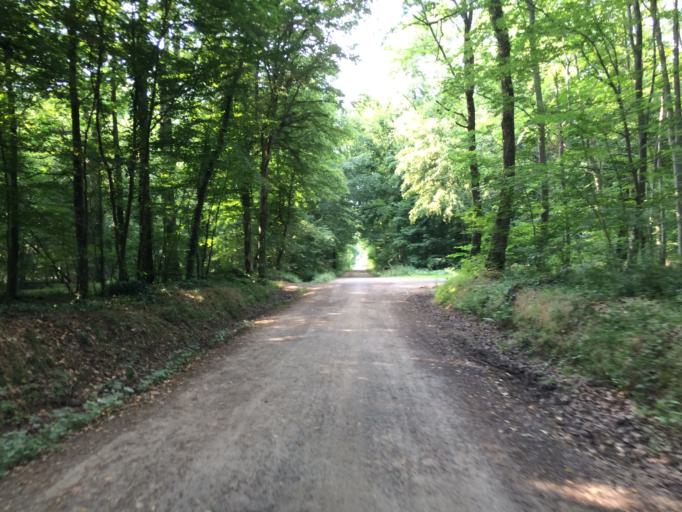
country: FR
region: Ile-de-France
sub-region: Departement de l'Essonne
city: Bievres
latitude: 48.7642
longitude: 2.2403
